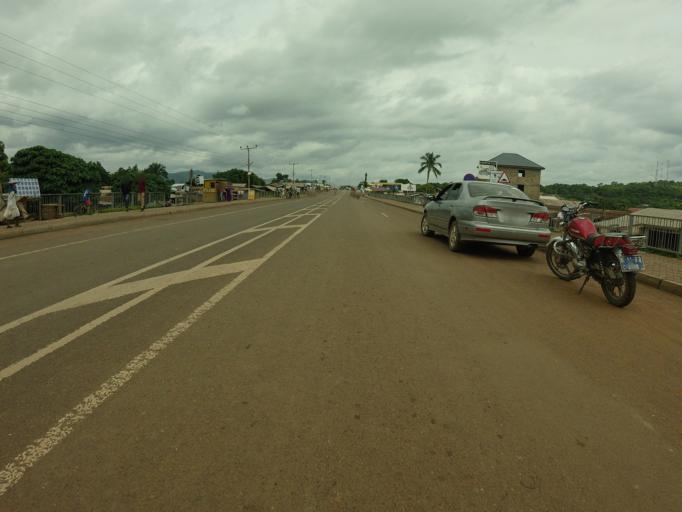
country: TG
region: Centrale
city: Sotouboua
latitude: 8.2662
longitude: 0.5199
